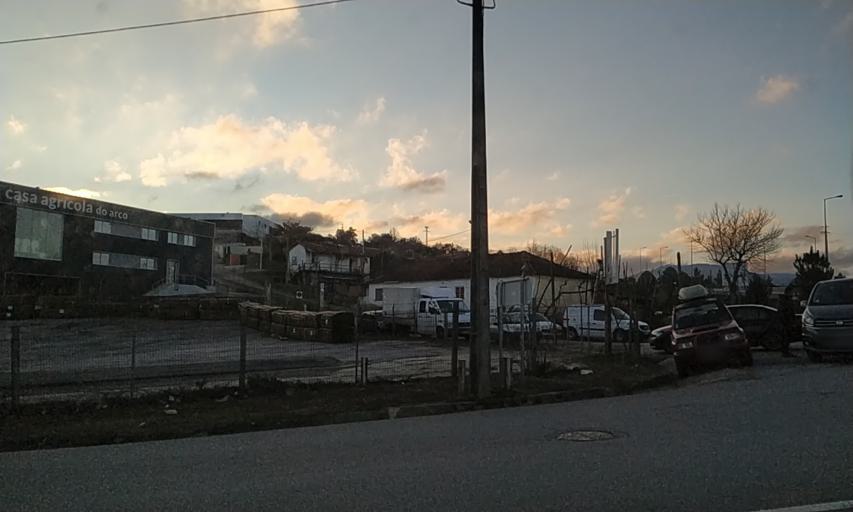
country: PT
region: Braga
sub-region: Cabeceiras de Basto
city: Cabeceiras de Basto
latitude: 41.4780
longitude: -7.9525
